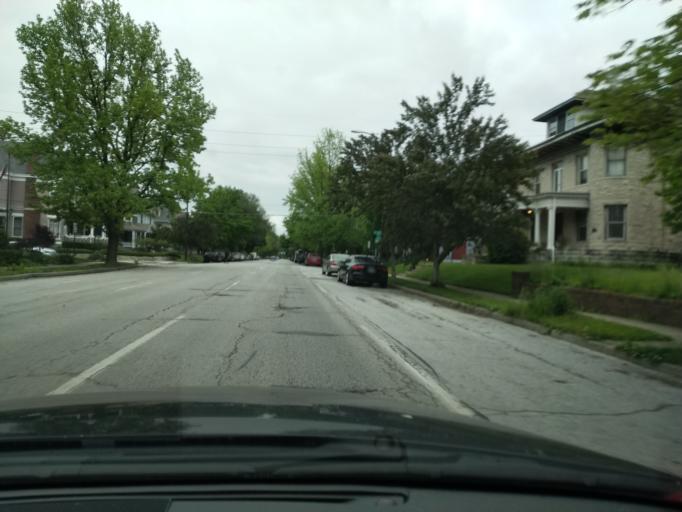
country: US
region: Indiana
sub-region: Marion County
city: Indianapolis
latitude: 39.7934
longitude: -86.1538
